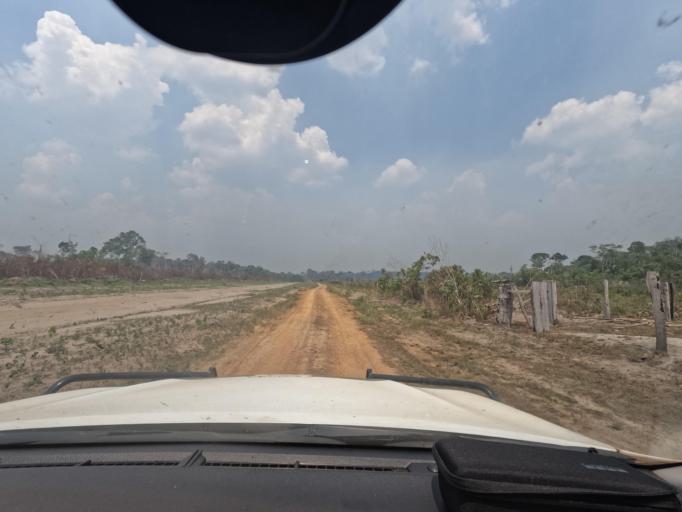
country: BR
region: Rondonia
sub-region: Porto Velho
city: Porto Velho
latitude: -8.7733
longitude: -63.1072
